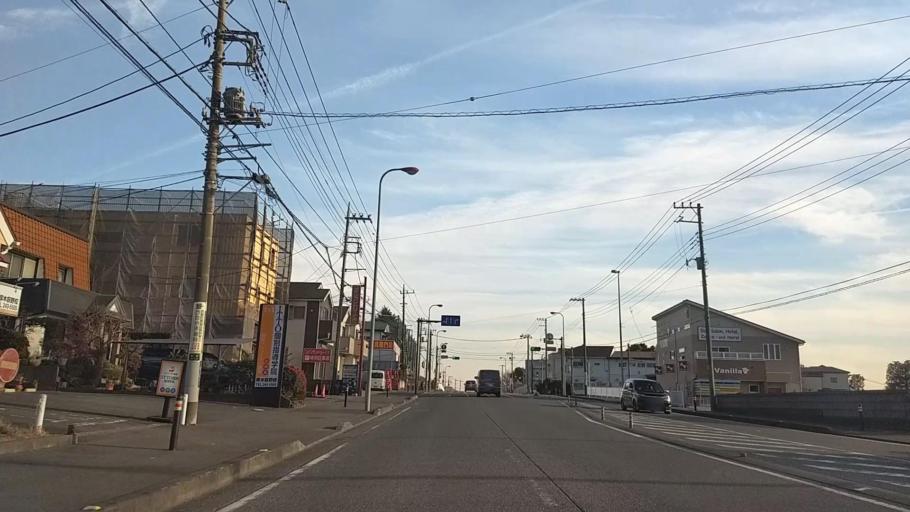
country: JP
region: Kanagawa
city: Atsugi
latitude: 35.4933
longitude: 139.3193
